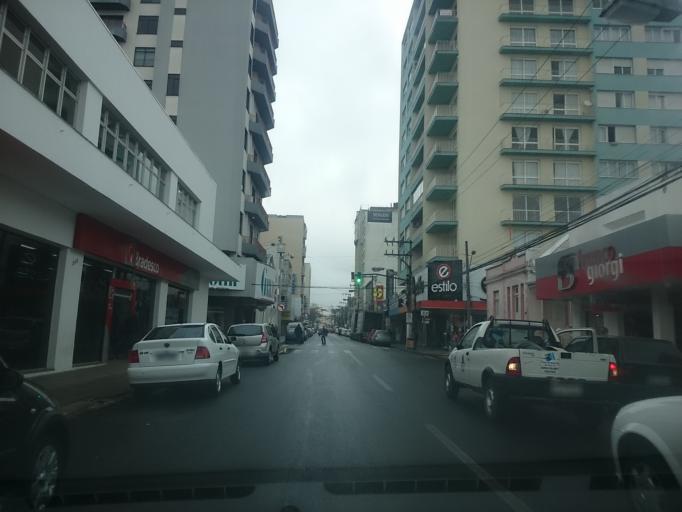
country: BR
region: Santa Catarina
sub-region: Lages
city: Lages
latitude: -27.8131
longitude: -50.3253
